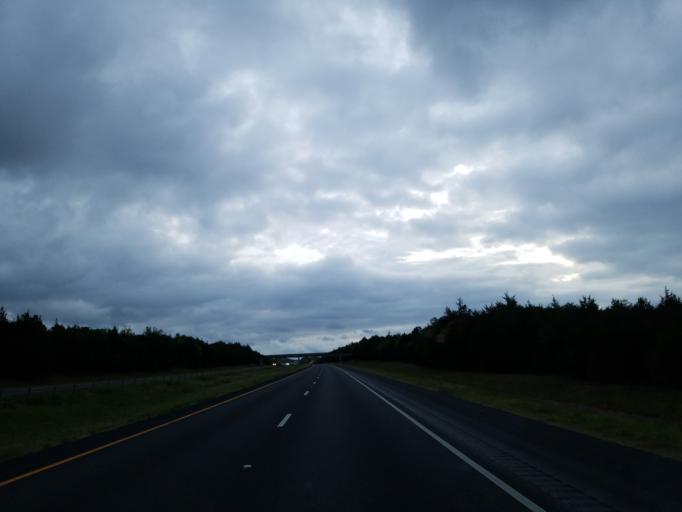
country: US
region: Alabama
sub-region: Sumter County
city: Livingston
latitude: 32.6834
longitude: -88.1616
